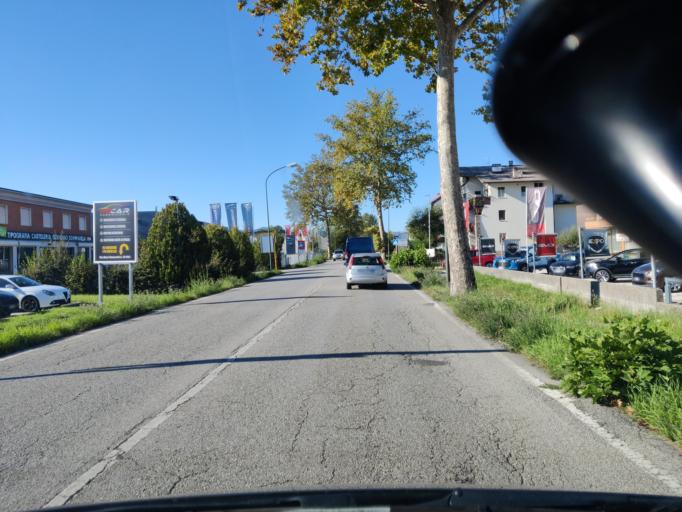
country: IT
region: Veneto
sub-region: Provincia di Belluno
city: Belluno
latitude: 46.1575
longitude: 12.2357
